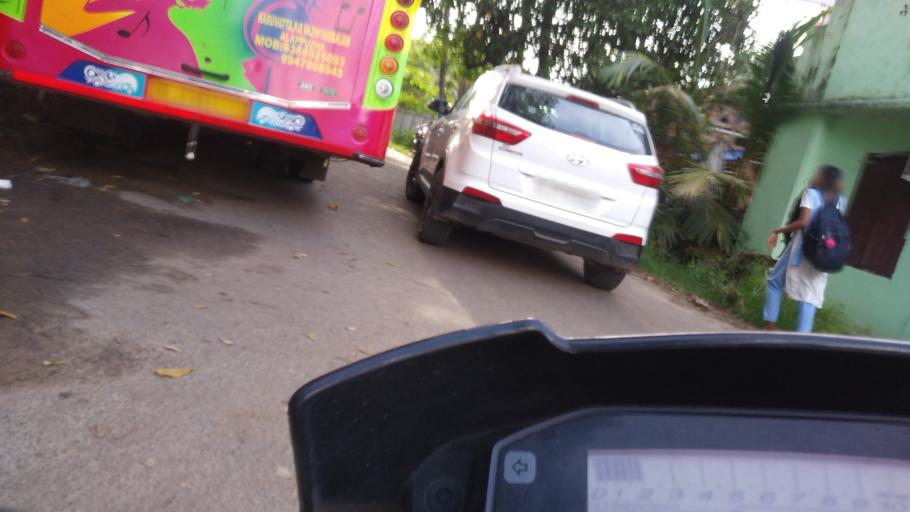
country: IN
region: Kerala
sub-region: Ernakulam
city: Cochin
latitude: 9.9918
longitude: 76.2662
